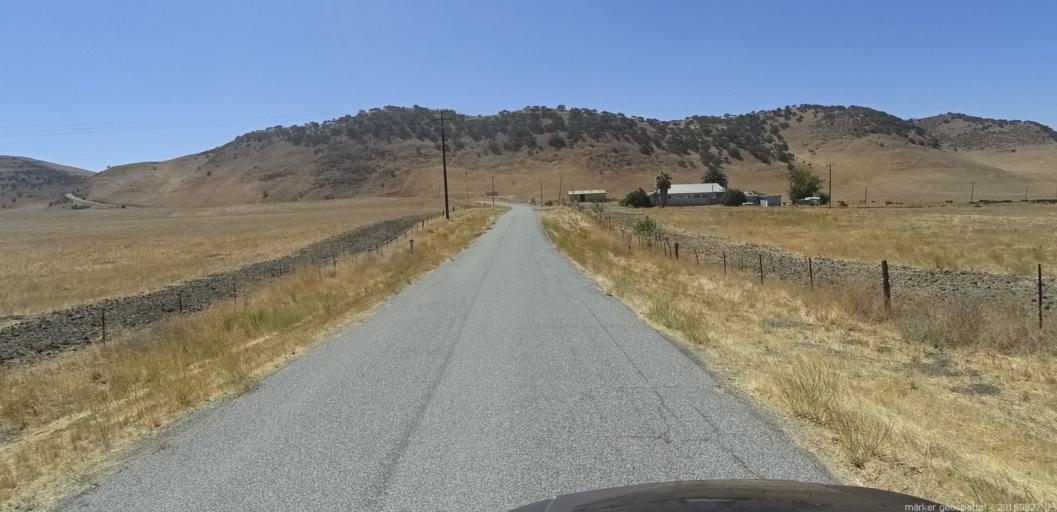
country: US
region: California
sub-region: Monterey County
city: King City
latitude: 36.1655
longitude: -120.8701
